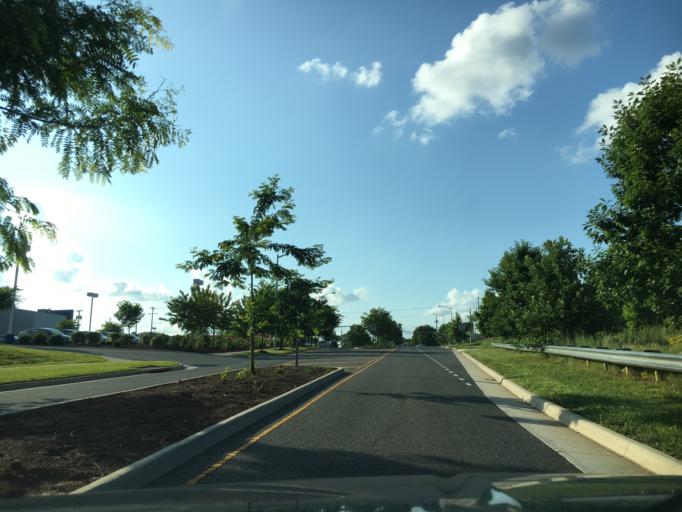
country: US
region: Virginia
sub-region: City of Lynchburg
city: West Lynchburg
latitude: 37.3944
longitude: -79.2274
